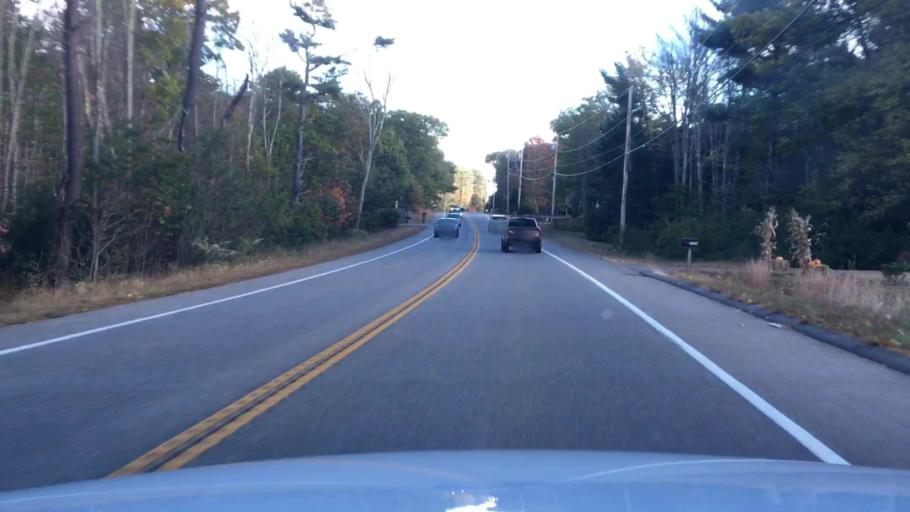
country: US
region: Maine
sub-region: York County
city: Wells Beach Station
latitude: 43.3377
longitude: -70.6345
